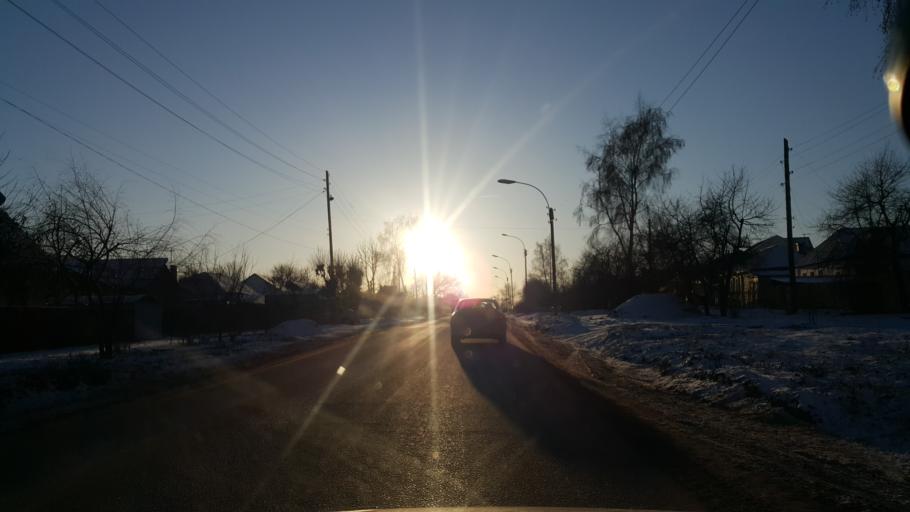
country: RU
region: Tambov
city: Pokrovo-Prigorodnoye
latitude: 52.7015
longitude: 41.4054
